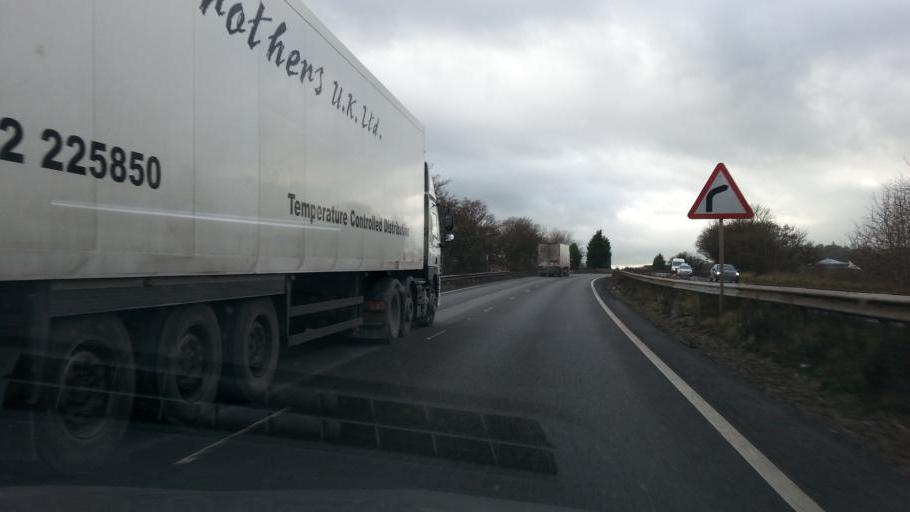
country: GB
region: England
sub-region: Staffordshire
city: Burton upon Trent
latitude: 52.8170
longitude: -1.6445
